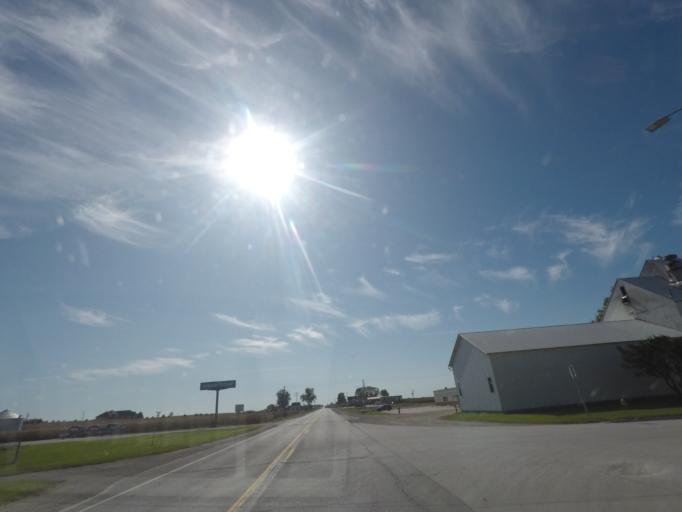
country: US
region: Iowa
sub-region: Story County
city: Nevada
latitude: 42.0176
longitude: -93.3095
